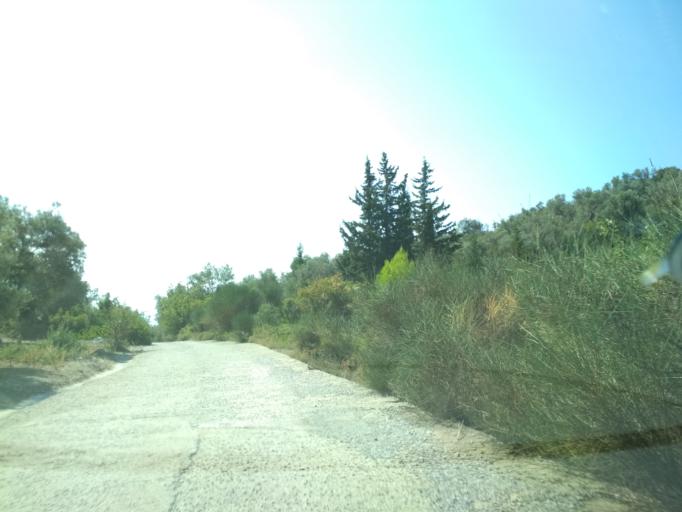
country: GR
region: Central Greece
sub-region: Nomos Evvoias
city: Oreoi
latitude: 38.8506
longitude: 23.1193
